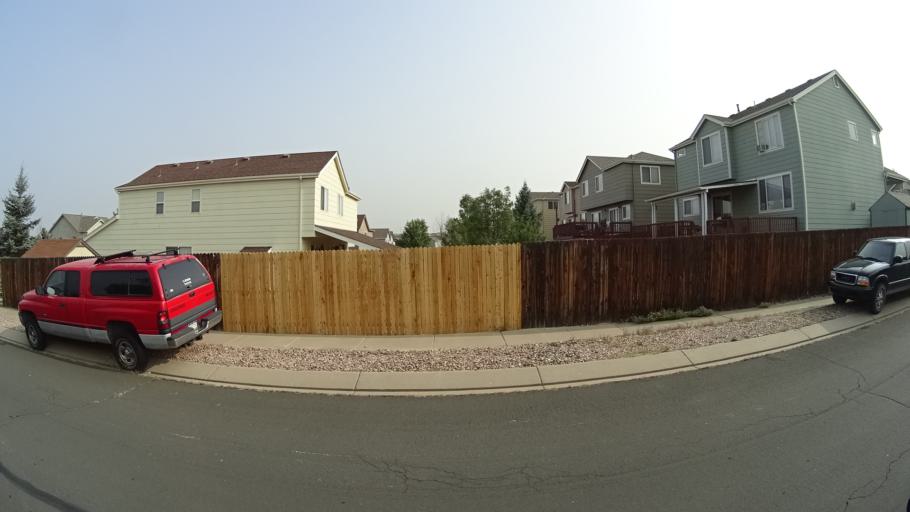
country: US
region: Colorado
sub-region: El Paso County
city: Cimarron Hills
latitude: 38.9322
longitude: -104.7323
